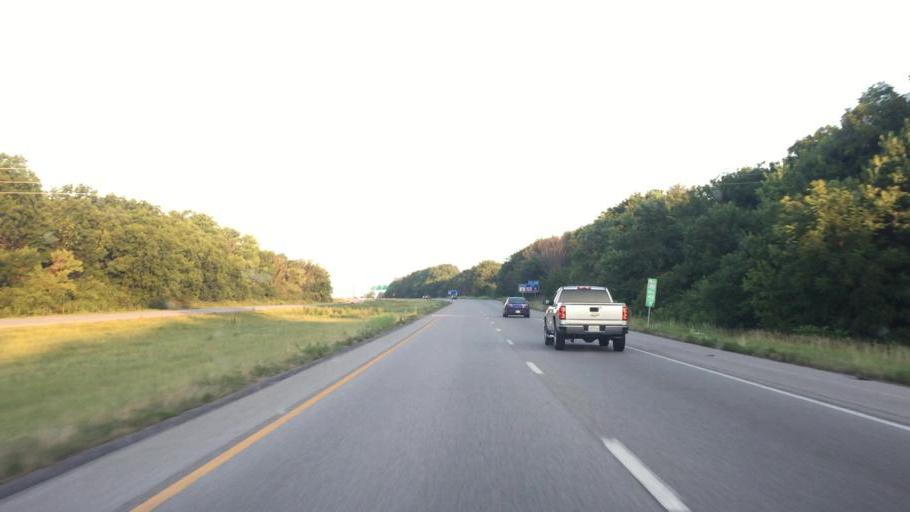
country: US
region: Missouri
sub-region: Clay County
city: Smithville
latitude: 39.3116
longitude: -94.5687
